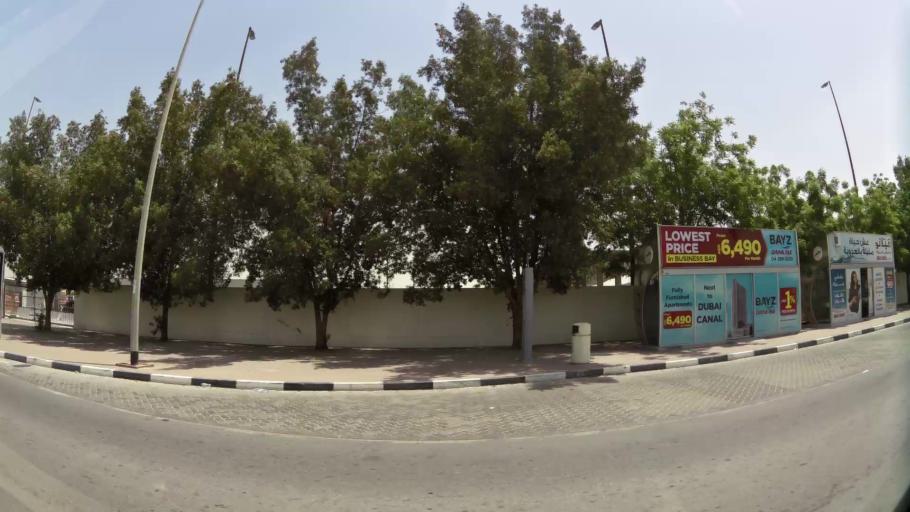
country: AE
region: Ash Shariqah
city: Sharjah
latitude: 25.2765
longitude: 55.4147
